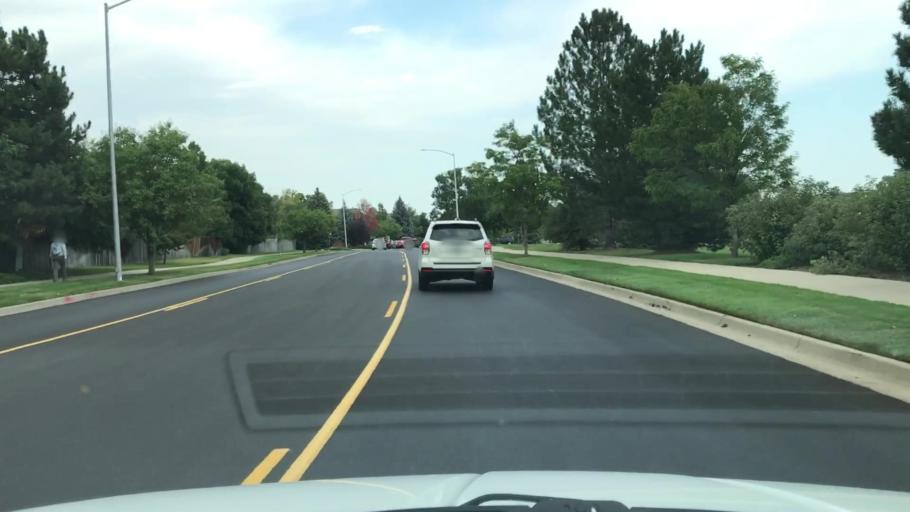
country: US
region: Colorado
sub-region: Broomfield County
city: Broomfield
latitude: 39.9336
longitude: -105.0859
